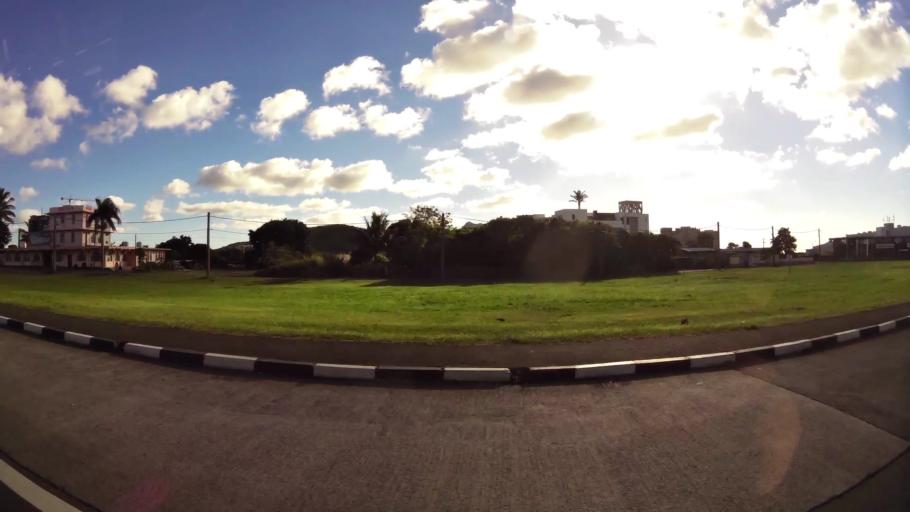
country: MU
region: Plaines Wilhems
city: Quatre Bornes
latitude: -20.2749
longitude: 57.4968
